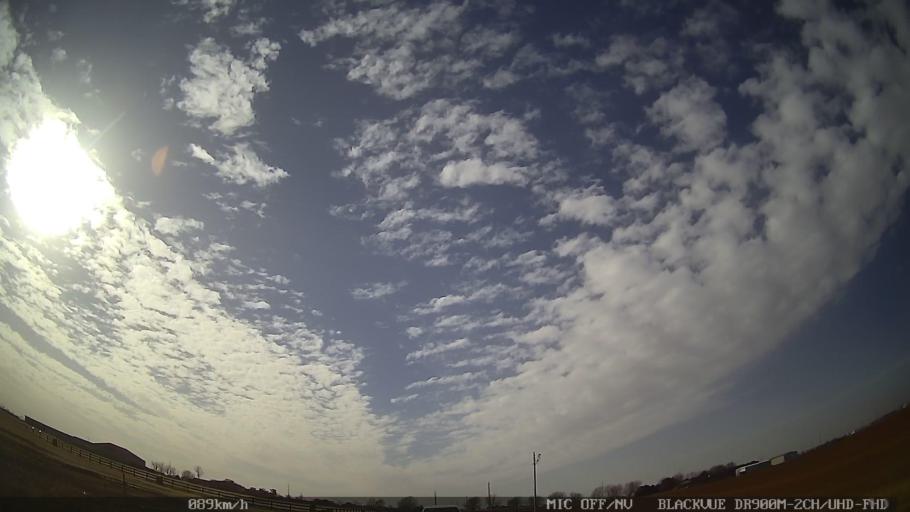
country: US
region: New Mexico
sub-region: Curry County
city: Clovis
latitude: 34.4193
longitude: -103.1328
